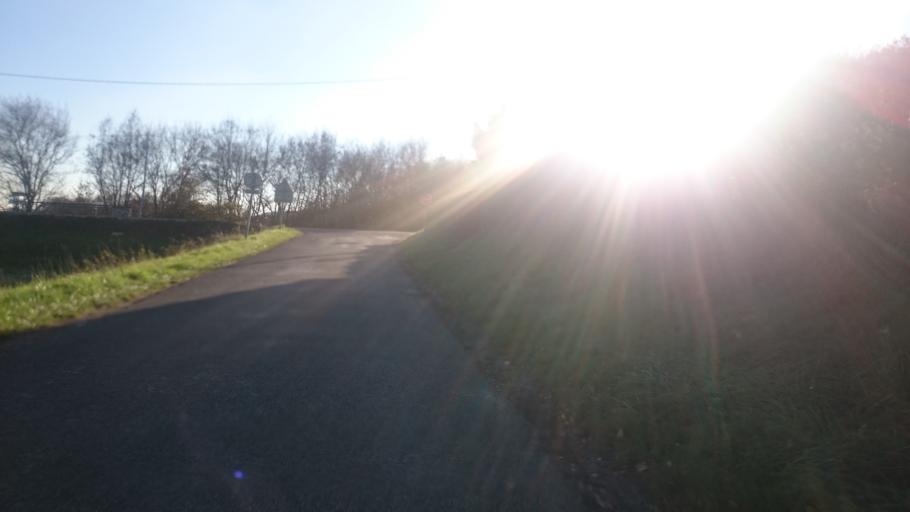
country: FR
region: Bourgogne
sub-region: Departement de Saone-et-Loire
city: Tournus
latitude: 46.5640
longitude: 4.9181
